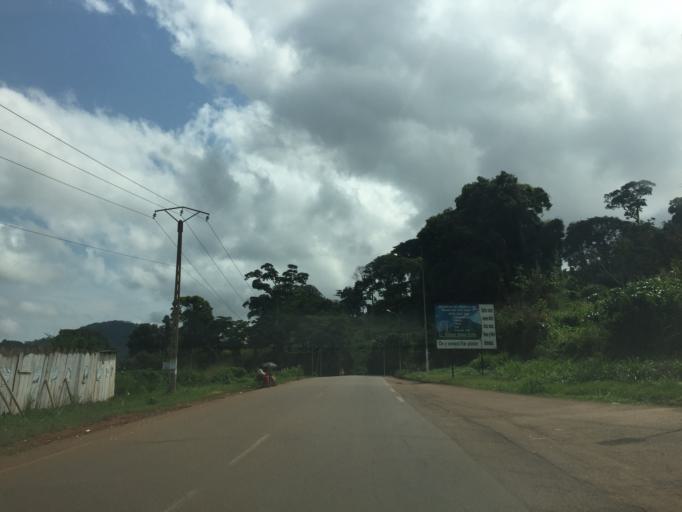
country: CM
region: Centre
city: Yaounde
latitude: 3.9123
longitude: 11.5020
